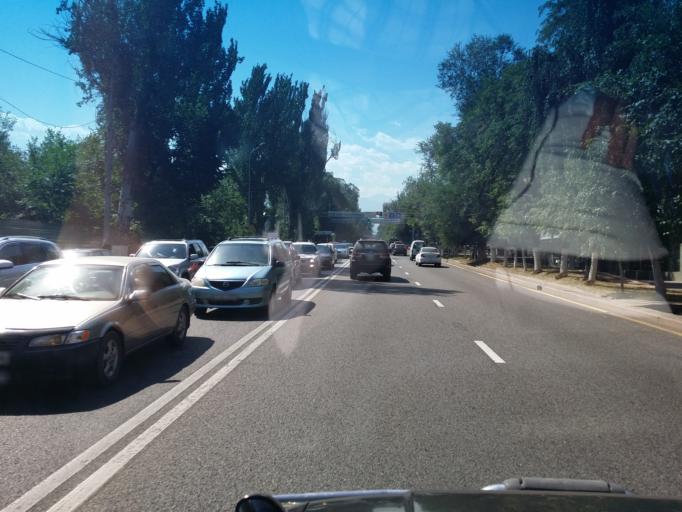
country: KZ
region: Almaty Qalasy
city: Almaty
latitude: 43.2685
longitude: 76.9450
